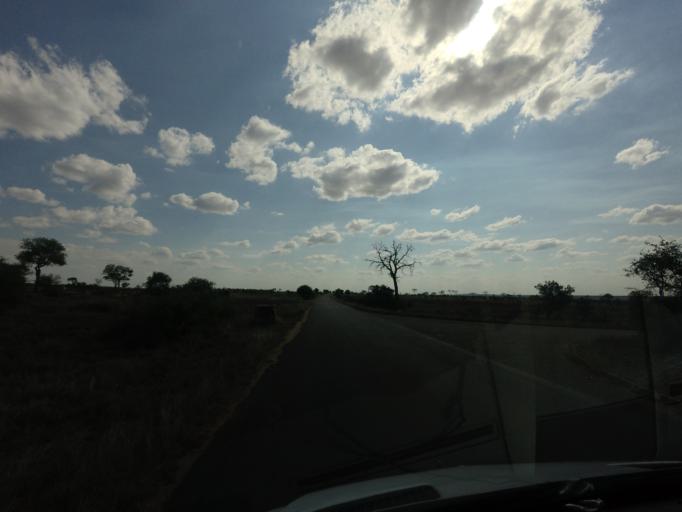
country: ZA
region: Limpopo
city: Thulamahashi
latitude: -24.3908
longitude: 31.6077
